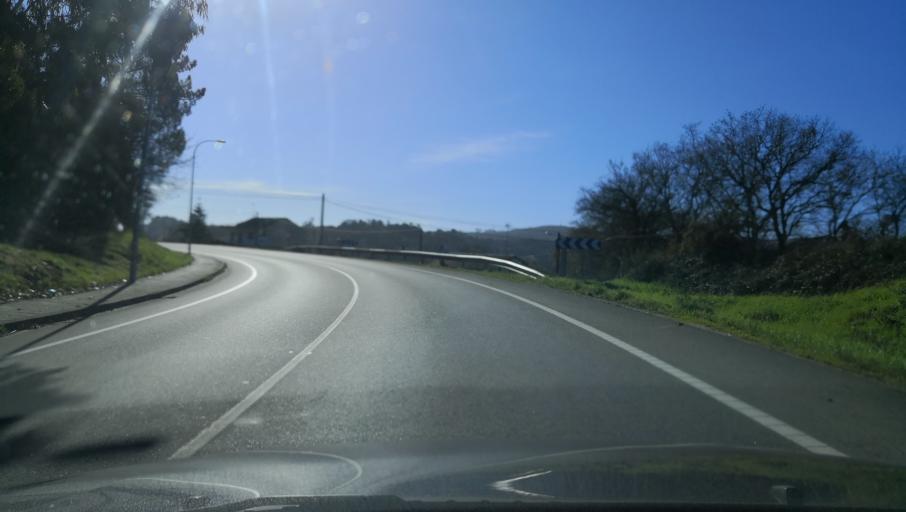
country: ES
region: Galicia
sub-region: Provincia de Pontevedra
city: Silleda
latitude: 42.7027
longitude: -8.2587
